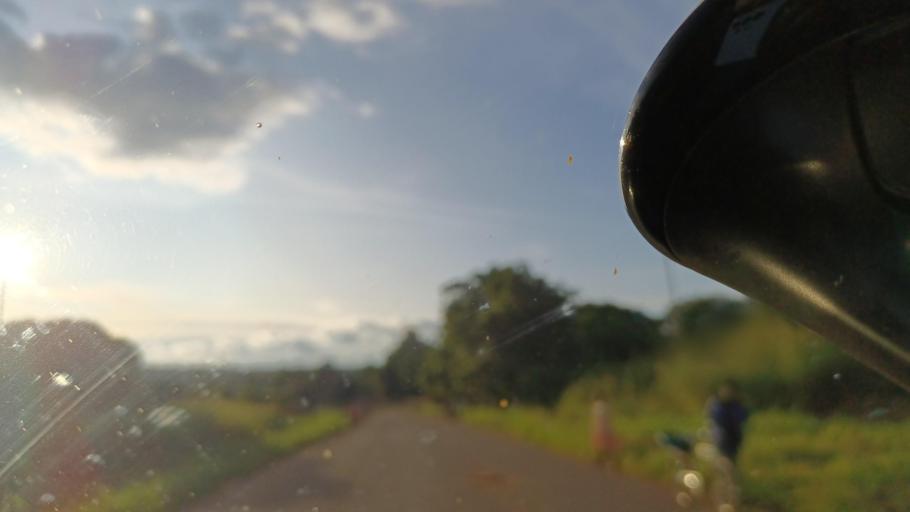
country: ZM
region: North-Western
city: Kasempa
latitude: -13.4594
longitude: 25.8489
